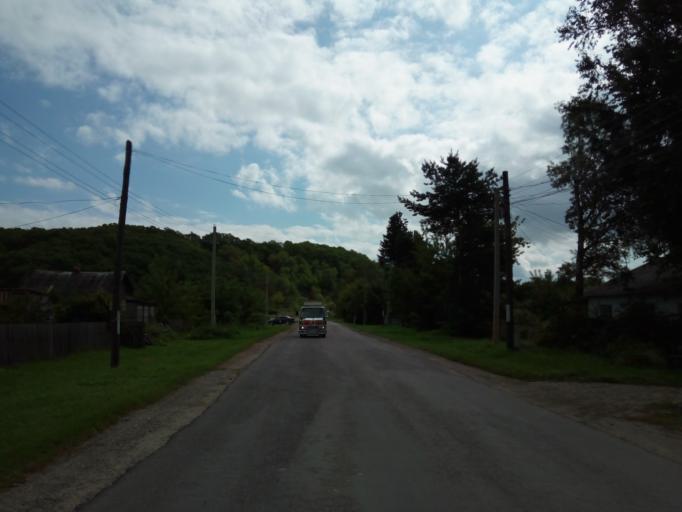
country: RU
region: Primorskiy
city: Dal'nerechensk
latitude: 45.9682
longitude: 133.7700
